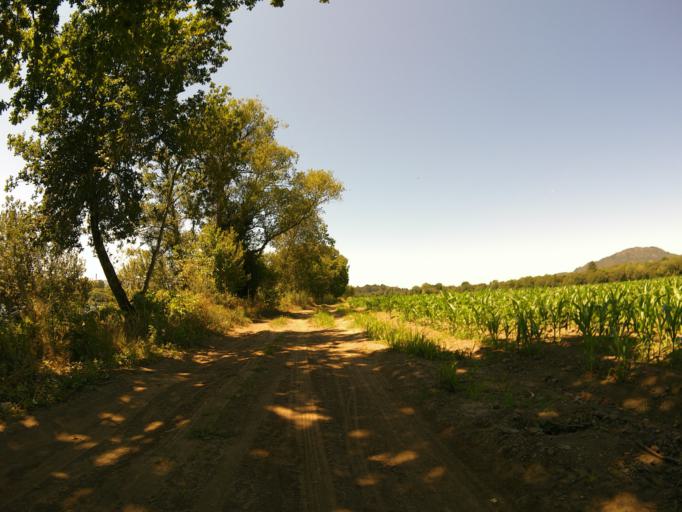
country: PT
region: Viana do Castelo
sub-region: Viana do Castelo
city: Darque
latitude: 41.7168
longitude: -8.7064
